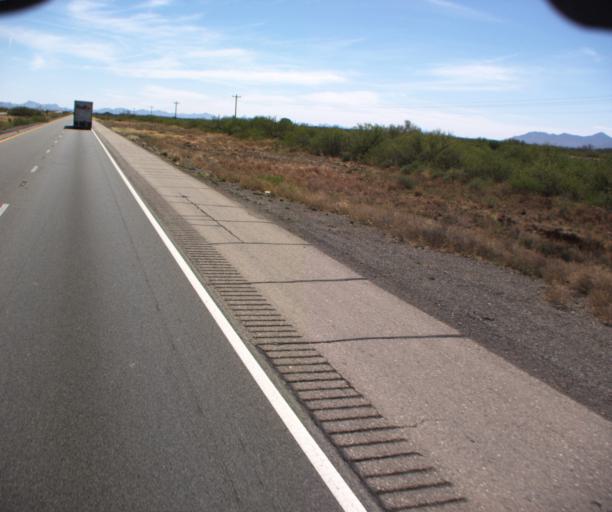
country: US
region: Arizona
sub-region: Cochise County
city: Willcox
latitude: 32.3100
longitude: -109.4104
